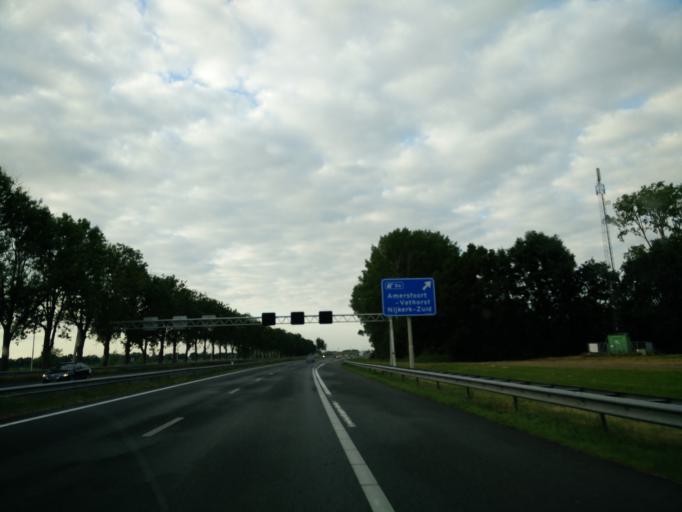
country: NL
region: Gelderland
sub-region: Gemeente Nijkerk
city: Nijkerk
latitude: 52.2035
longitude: 5.4394
